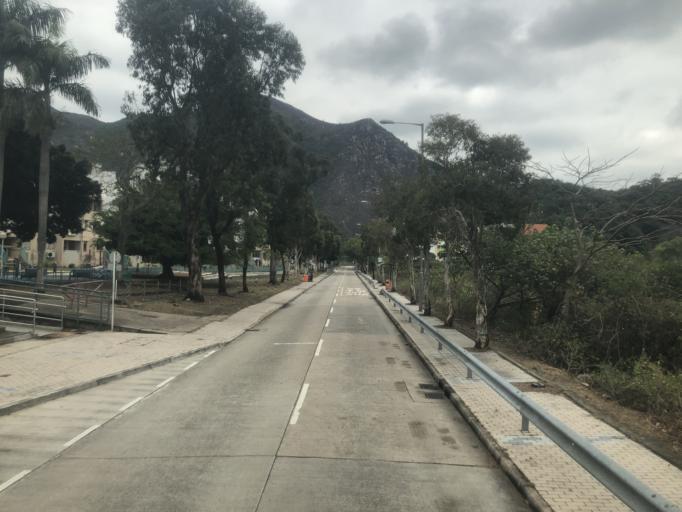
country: HK
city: Tai O
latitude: 22.2525
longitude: 113.8644
